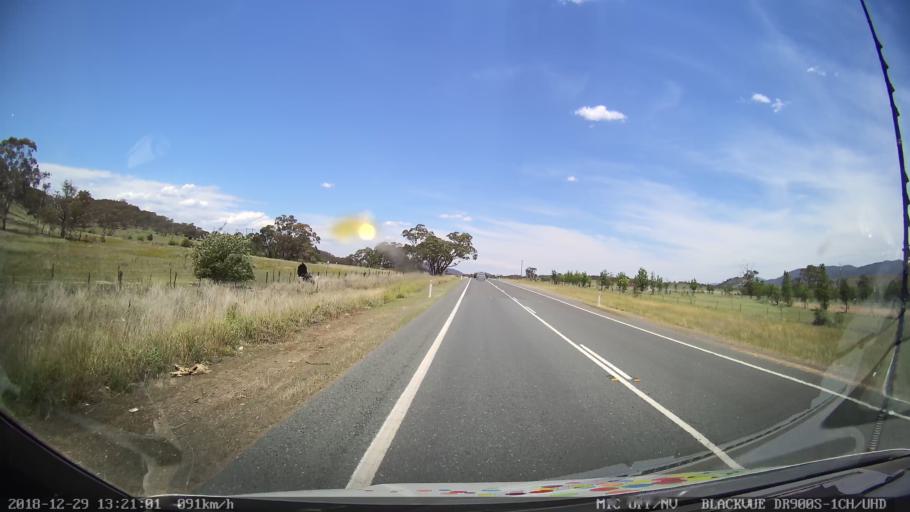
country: AU
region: Australian Capital Territory
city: Macarthur
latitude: -35.7867
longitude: 149.1630
